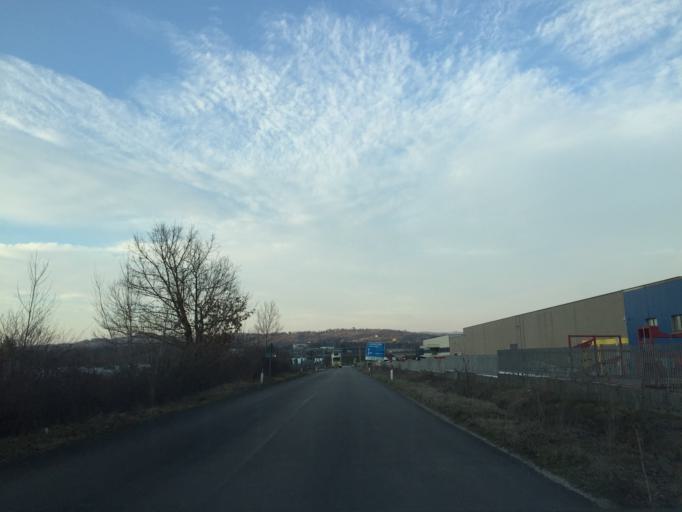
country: IT
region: Molise
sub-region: Provincia di Campobasso
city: Guardiaregia
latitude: 41.4596
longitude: 14.5571
